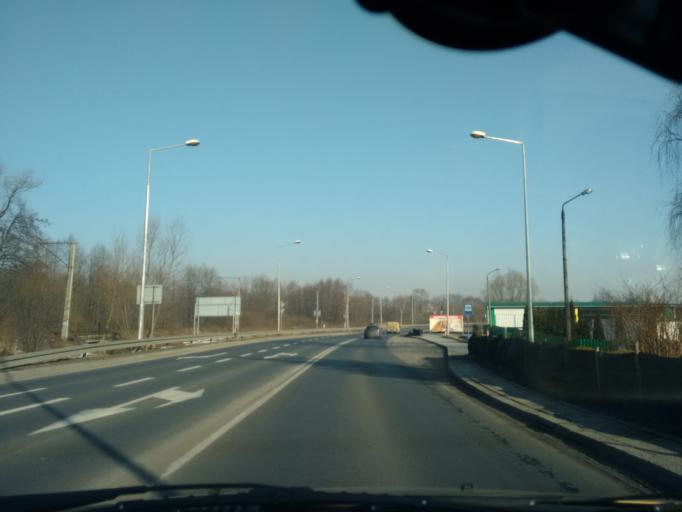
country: PL
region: Lesser Poland Voivodeship
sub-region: Powiat wadowicki
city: Wadowice
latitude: 49.8900
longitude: 19.4920
